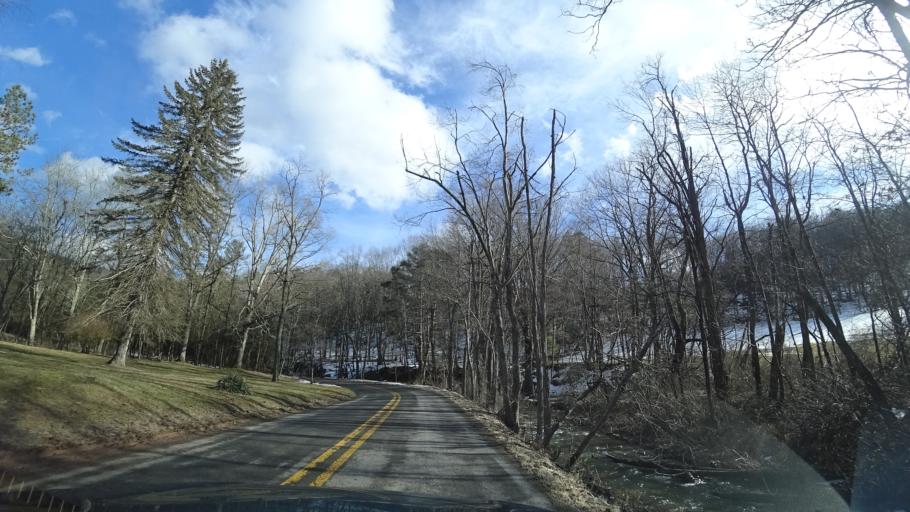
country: US
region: Virginia
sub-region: Shenandoah County
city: Basye
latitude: 38.8890
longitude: -78.8984
